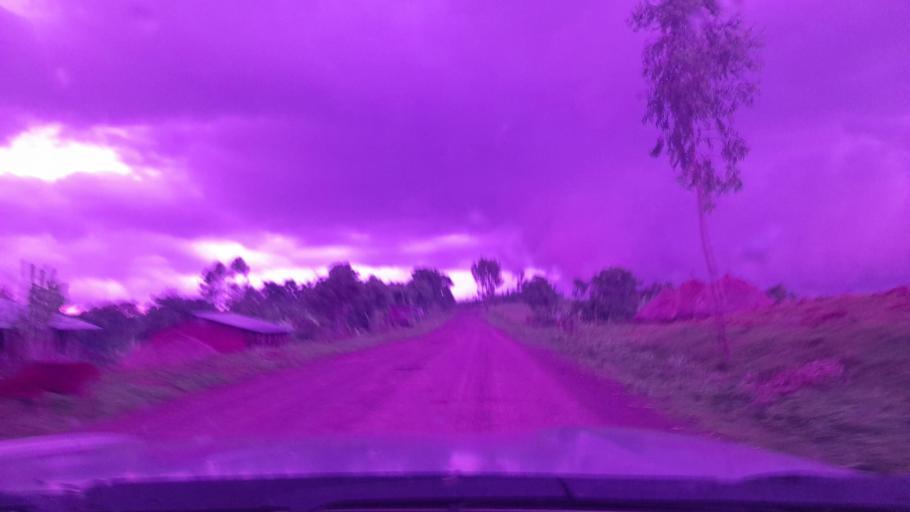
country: ET
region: Southern Nations, Nationalities, and People's Region
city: Mizan Teferi
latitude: 6.9115
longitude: 35.8422
